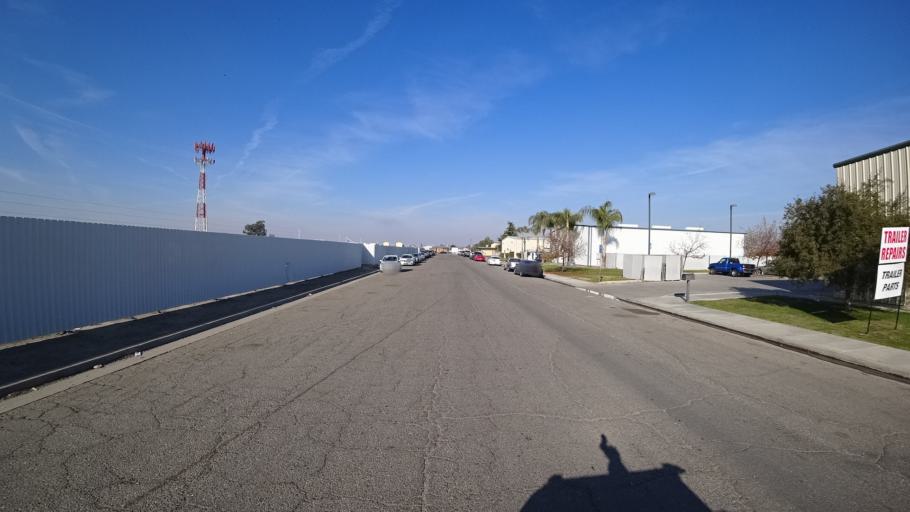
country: US
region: California
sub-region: Kern County
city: Bakersfield
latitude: 35.3233
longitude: -118.9997
